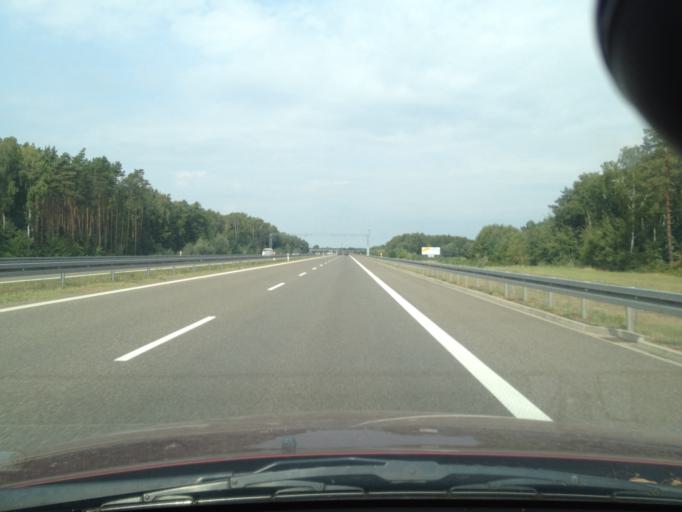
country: PL
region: West Pomeranian Voivodeship
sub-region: Powiat mysliborski
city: Nowogrodek Pomorski
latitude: 52.9330
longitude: 14.9835
